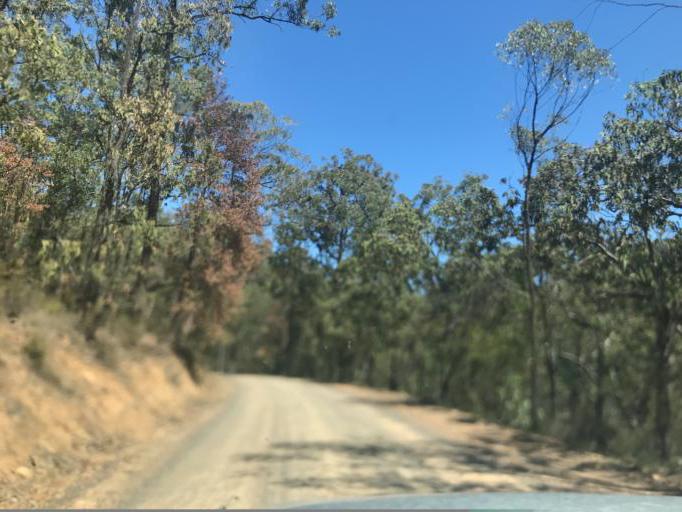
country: AU
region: New South Wales
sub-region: Wyong Shire
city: Little Jilliby
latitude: -33.1861
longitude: 151.0521
